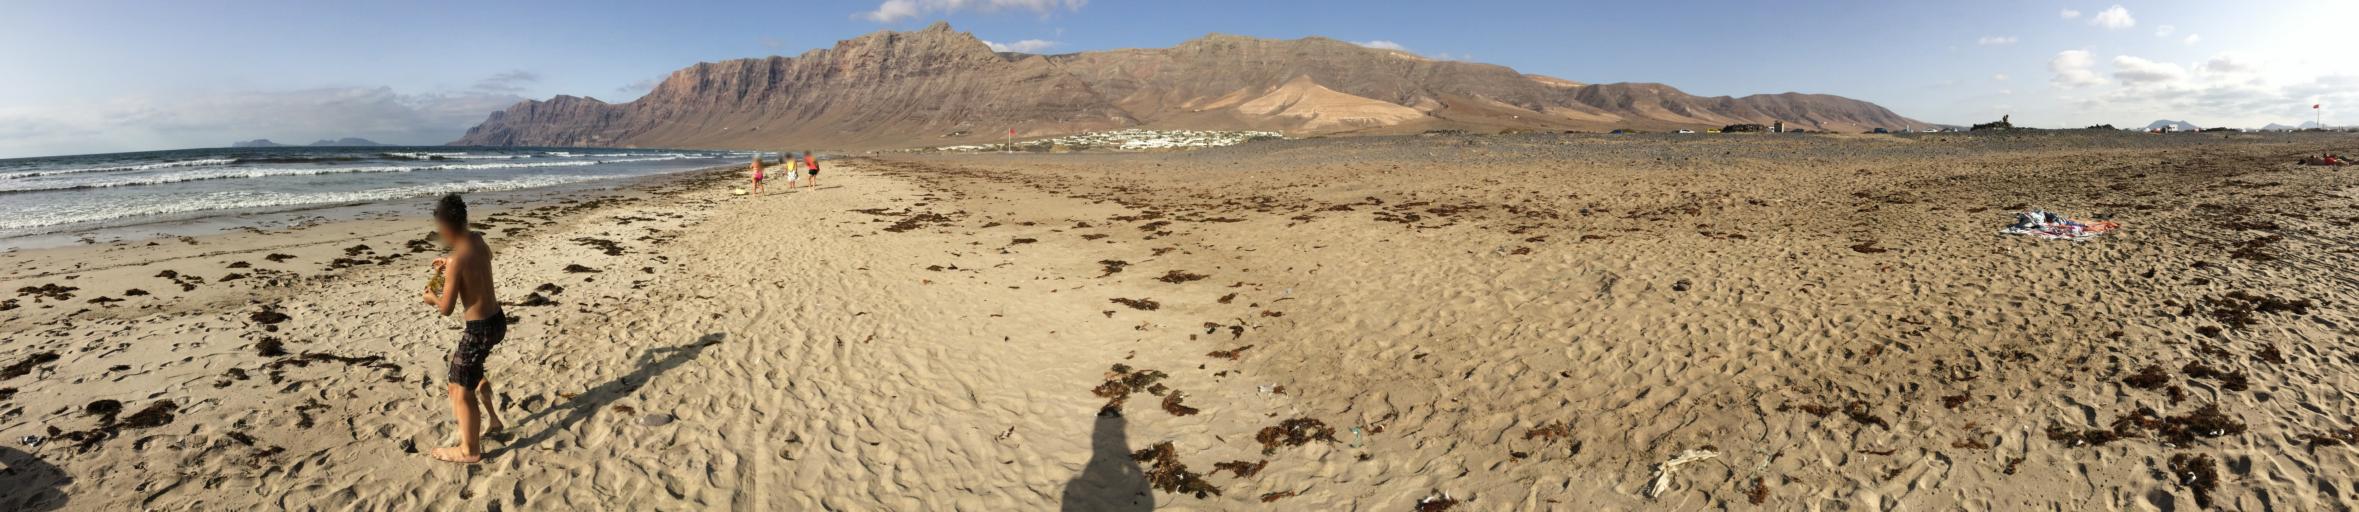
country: ES
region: Canary Islands
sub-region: Provincia de Las Palmas
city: Teguise
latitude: 29.1162
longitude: -13.5544
